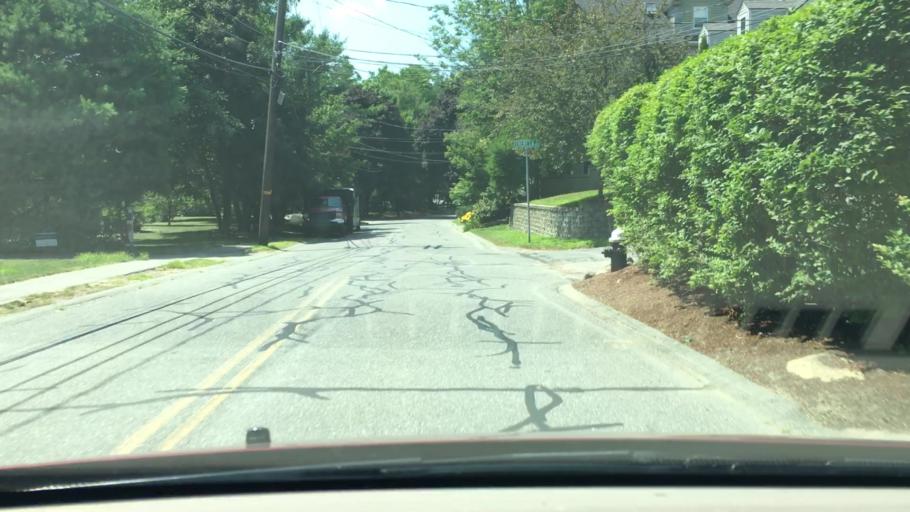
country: US
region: Massachusetts
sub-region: Middlesex County
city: Belmont
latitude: 42.4277
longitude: -71.1937
